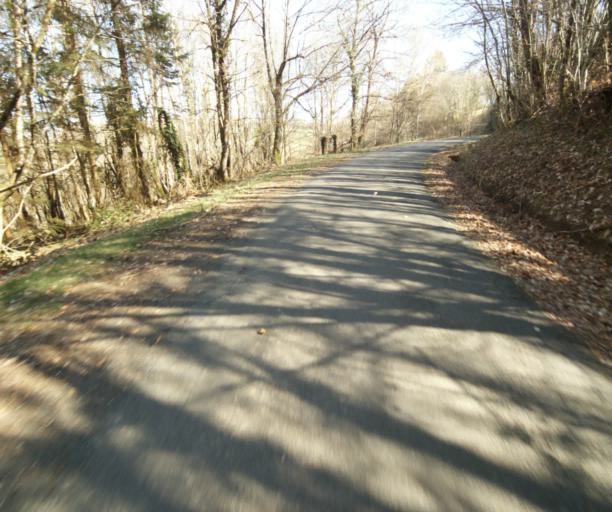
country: FR
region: Limousin
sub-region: Departement de la Correze
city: Chamboulive
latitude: 45.4232
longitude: 1.6610
